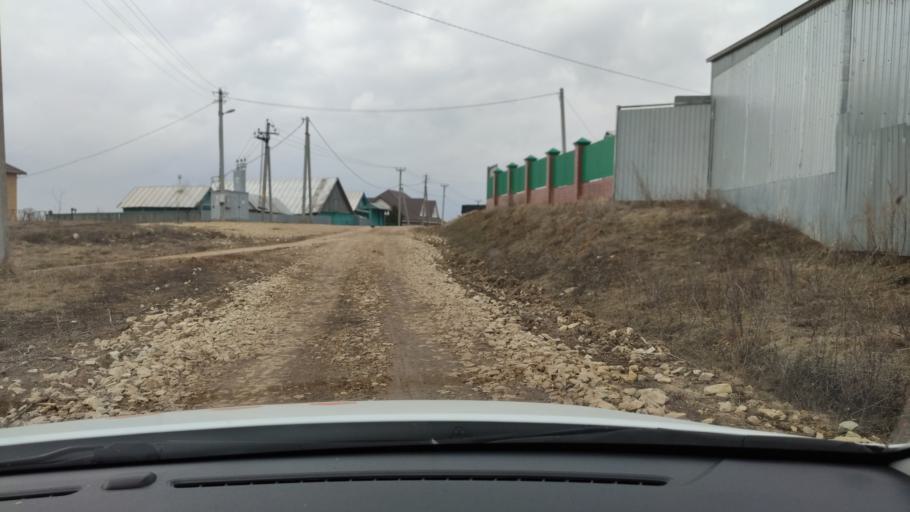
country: RU
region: Tatarstan
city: Vysokaya Gora
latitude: 56.2105
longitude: 49.3139
